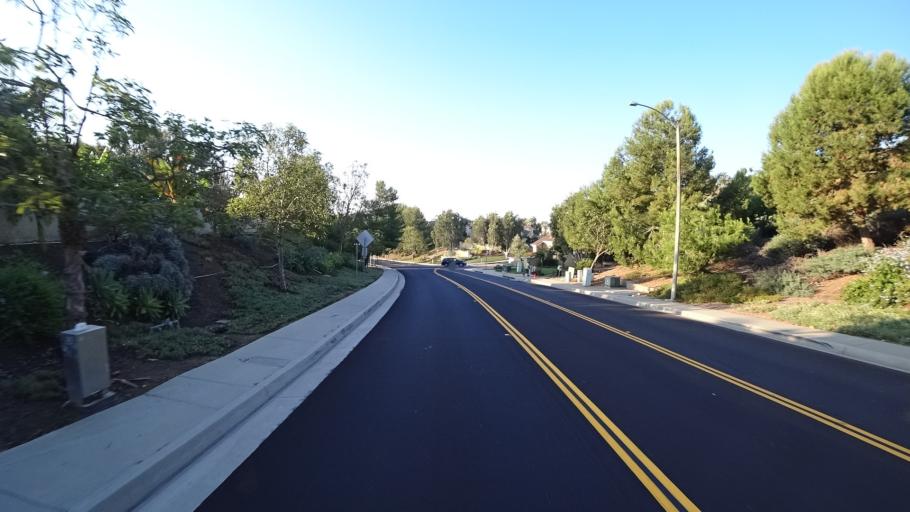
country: US
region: California
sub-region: Orange County
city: San Juan Capistrano
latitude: 33.4704
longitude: -117.6369
